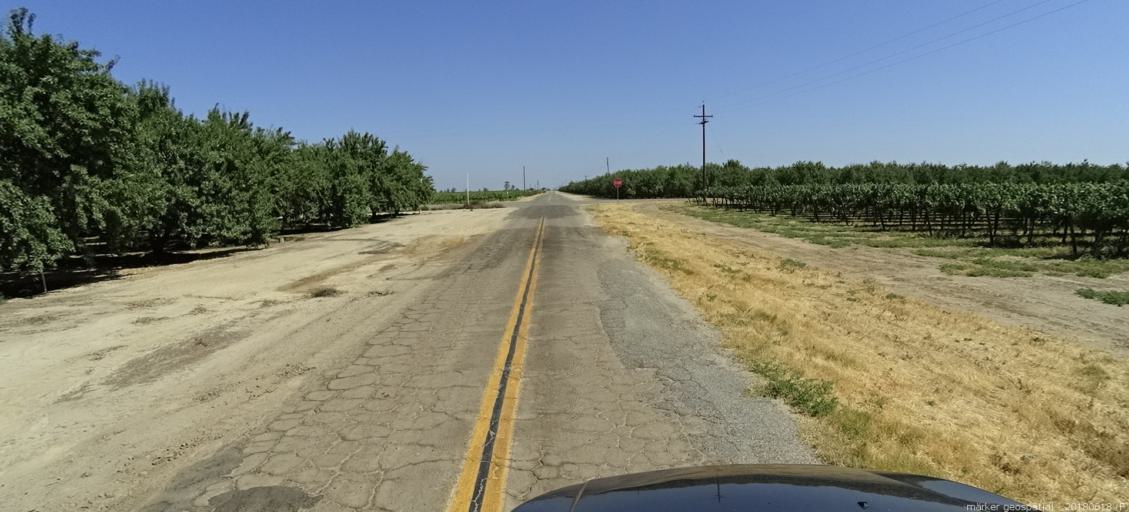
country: US
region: California
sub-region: Madera County
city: Parkwood
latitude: 36.8504
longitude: -120.1828
